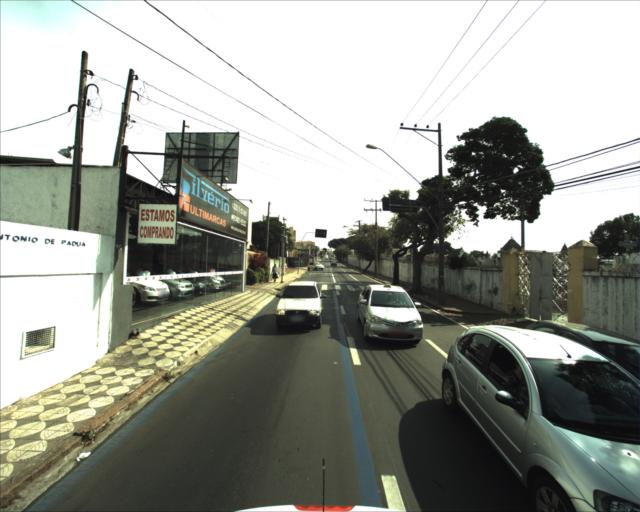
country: BR
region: Sao Paulo
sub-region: Sorocaba
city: Sorocaba
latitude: -23.4906
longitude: -47.4617
